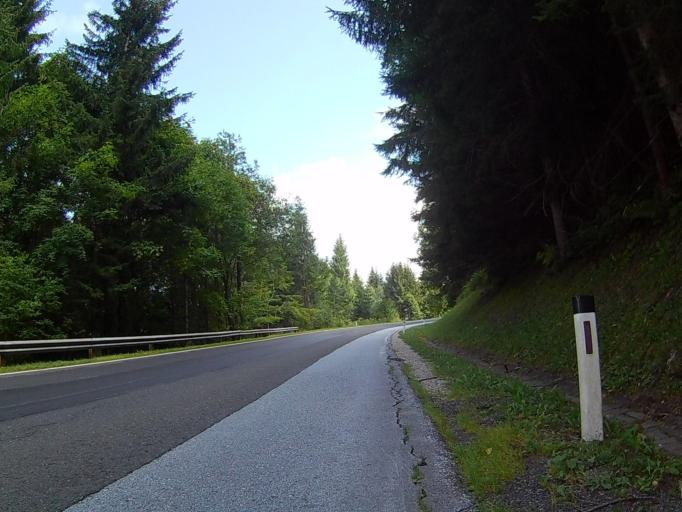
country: AT
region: Styria
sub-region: Politischer Bezirk Deutschlandsberg
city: Soboth
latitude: 46.7029
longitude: 15.0948
